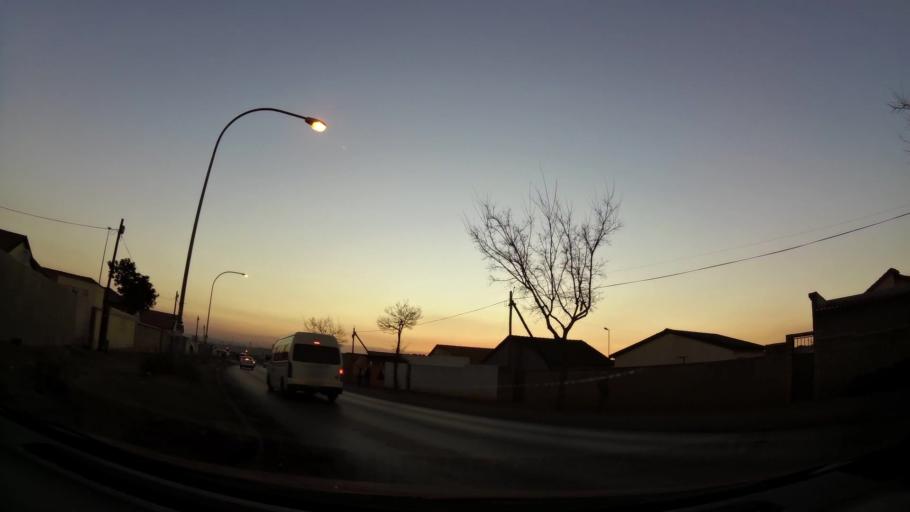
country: ZA
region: Gauteng
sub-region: City of Johannesburg Metropolitan Municipality
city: Soweto
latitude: -26.2344
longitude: 27.8271
